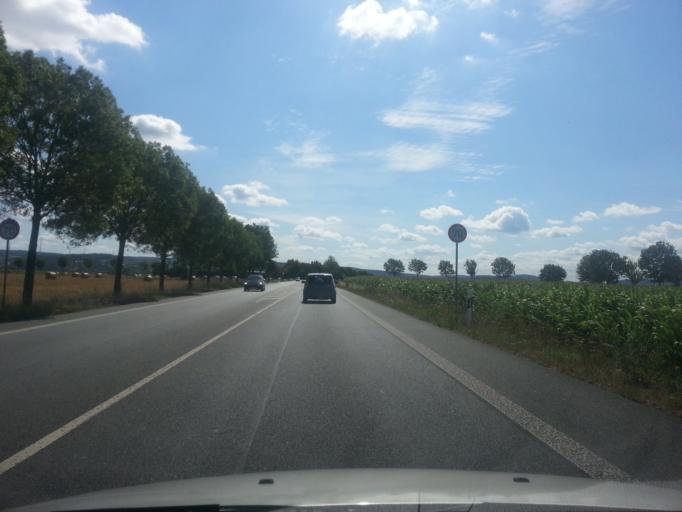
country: DE
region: Hesse
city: Gross-Umstadt
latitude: 49.8810
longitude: 8.8979
